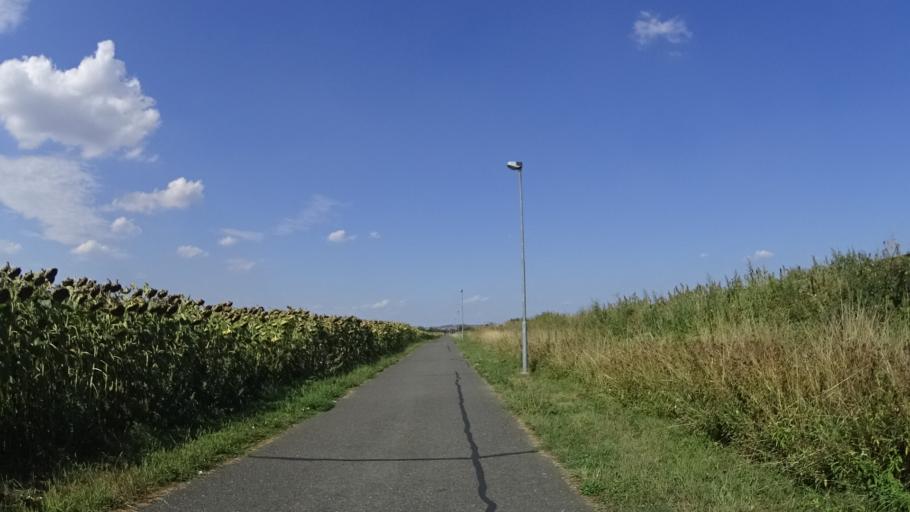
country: CZ
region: Zlin
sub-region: Okres Zlin
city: Ostrozska Nova Ves
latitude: 49.0235
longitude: 17.4510
